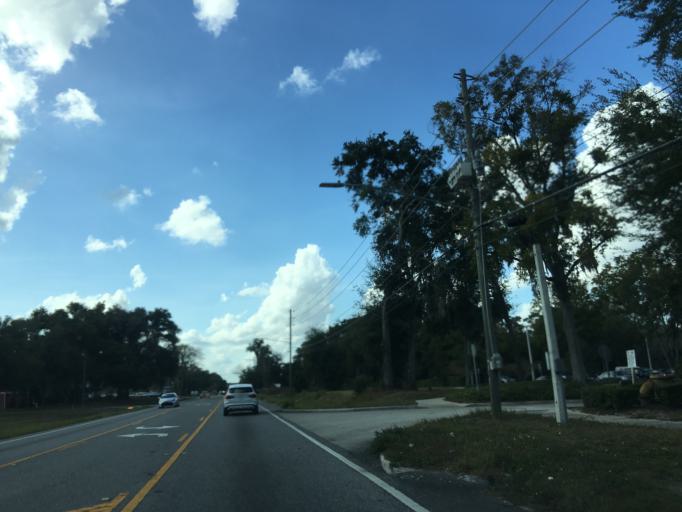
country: US
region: Florida
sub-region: Orange County
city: Eatonville
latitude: 28.6185
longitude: -81.3995
